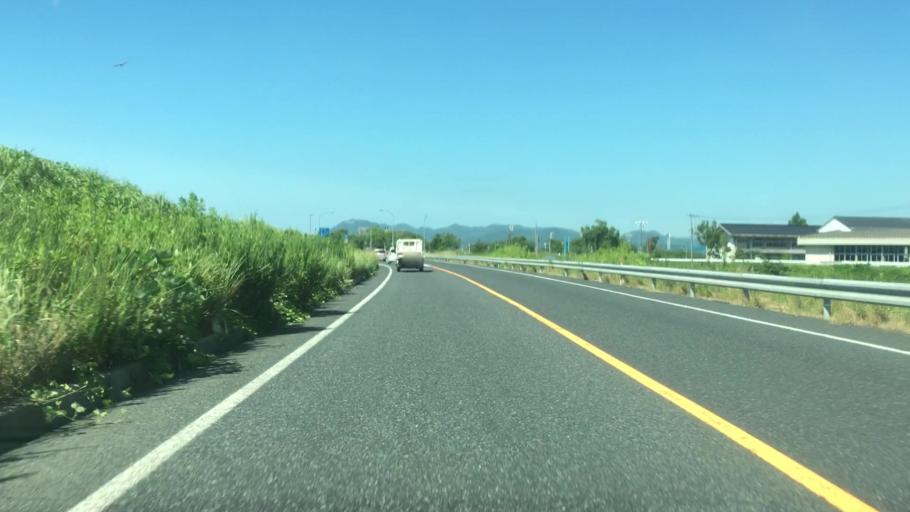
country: JP
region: Tottori
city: Tottori
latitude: 35.4490
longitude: 134.2137
